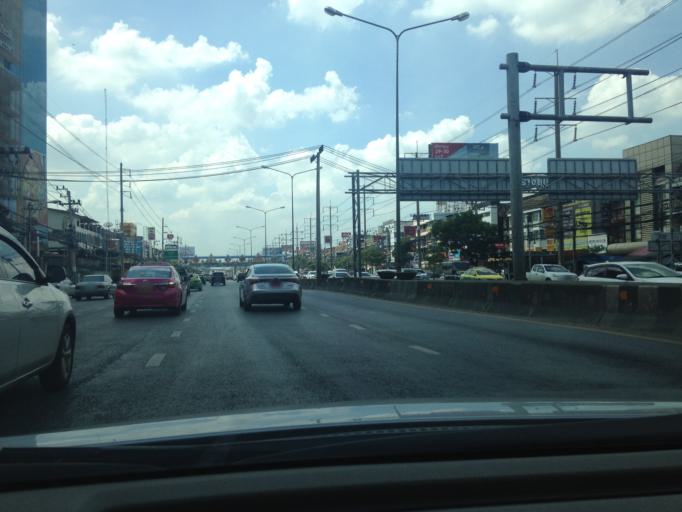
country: TH
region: Phra Nakhon Si Ayutthaya
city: Ban Bang Kadi Pathum Thani
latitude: 13.9874
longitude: 100.6105
